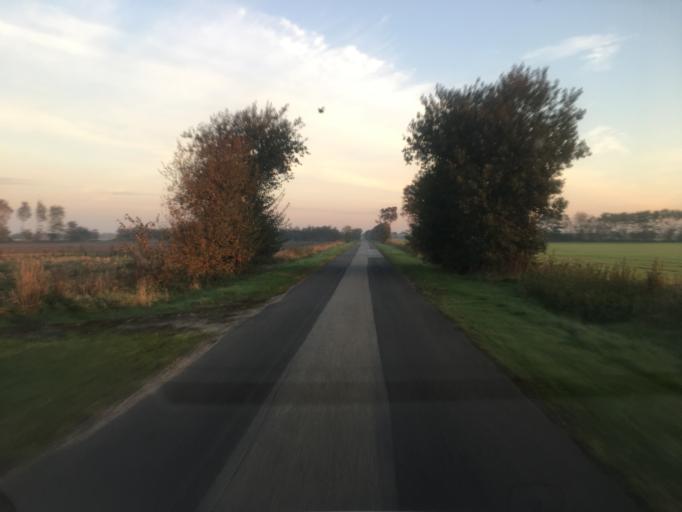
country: DK
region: South Denmark
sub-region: Tonder Kommune
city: Logumkloster
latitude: 55.0564
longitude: 9.0238
